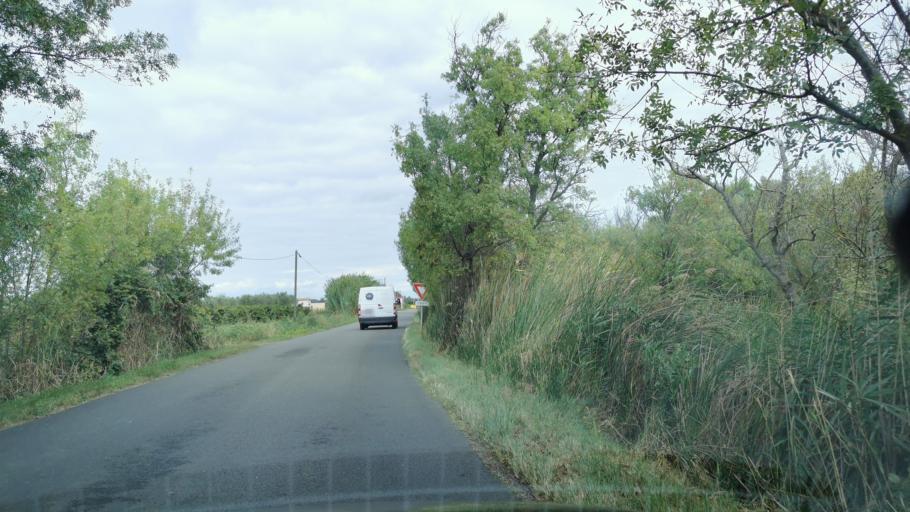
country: FR
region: Languedoc-Roussillon
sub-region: Departement de l'Herault
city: Lespignan
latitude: 43.2315
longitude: 3.1933
